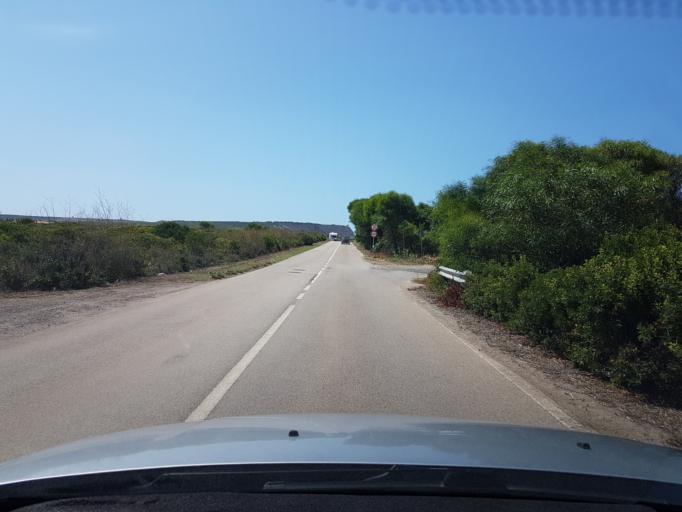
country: IT
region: Sardinia
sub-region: Provincia di Oristano
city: Riola Sardo
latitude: 40.0405
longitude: 8.4075
